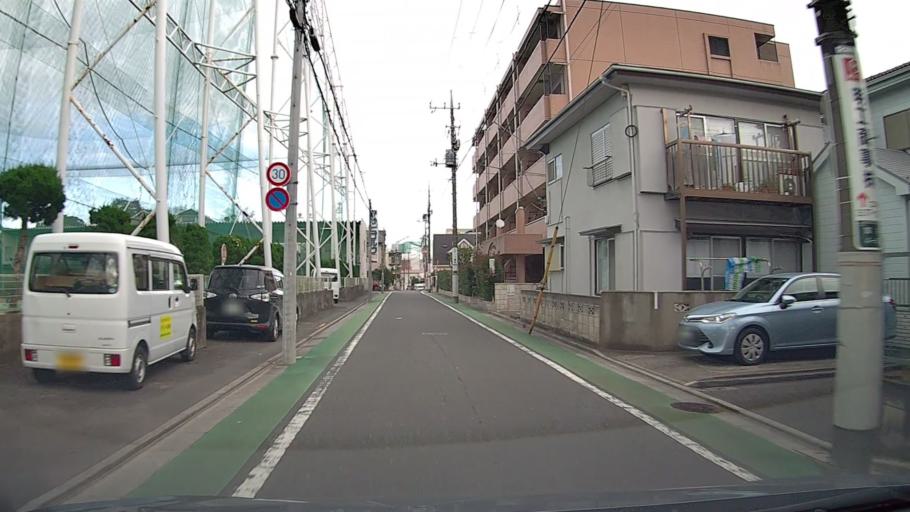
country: JP
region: Saitama
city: Wako
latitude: 35.7439
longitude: 139.6257
